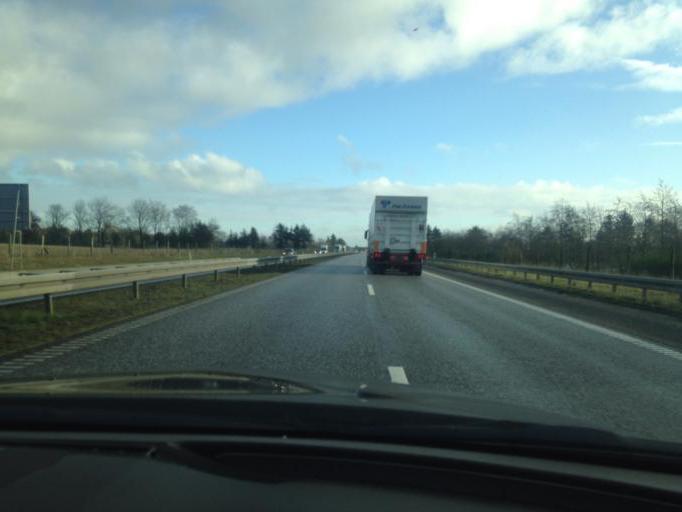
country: DK
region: South Denmark
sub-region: Vejen Kommune
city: Vejen
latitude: 55.4933
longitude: 9.1450
